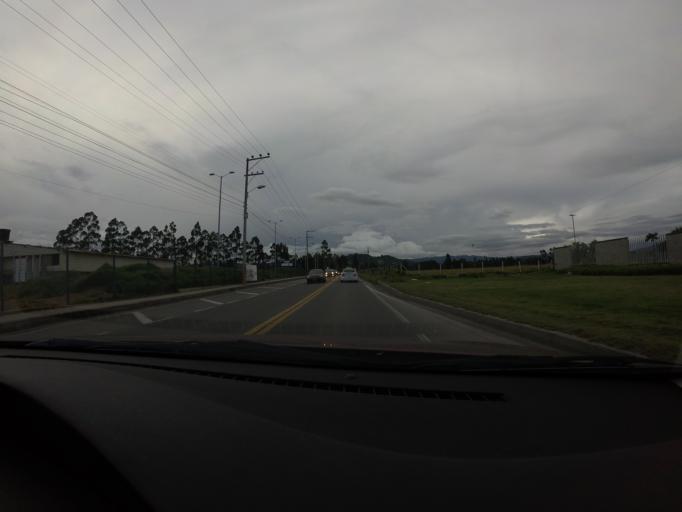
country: CO
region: Cundinamarca
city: Sopo
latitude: 4.9221
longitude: -73.9490
